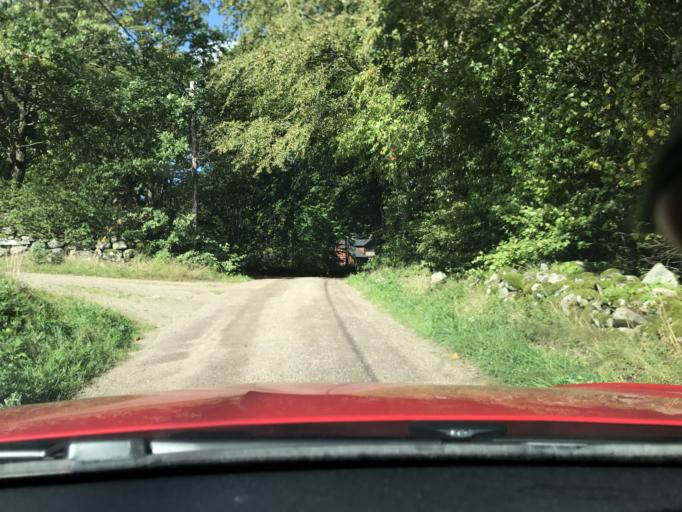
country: SE
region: Skane
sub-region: Hassleholms Kommun
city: Sosdala
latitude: 56.0029
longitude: 13.7040
